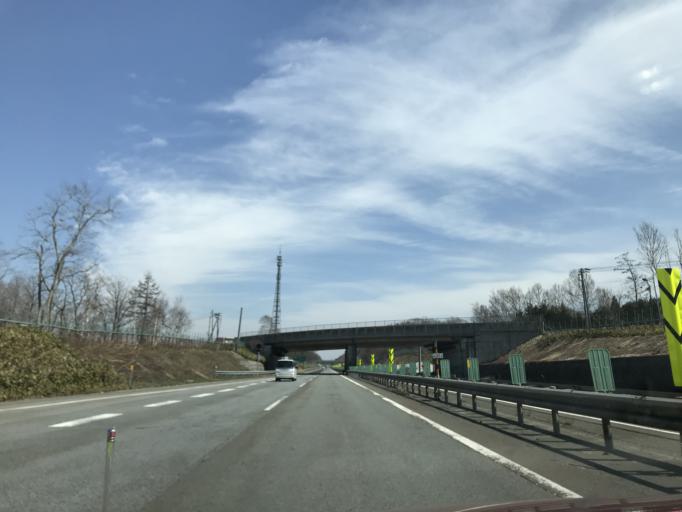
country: JP
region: Hokkaido
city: Iwamizawa
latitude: 43.1771
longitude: 141.7708
